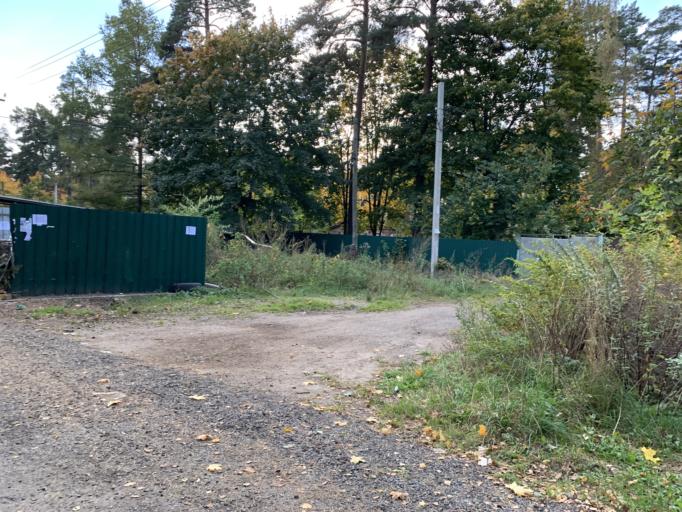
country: RU
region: Moskovskaya
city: Mamontovka
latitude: 55.9789
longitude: 37.8326
